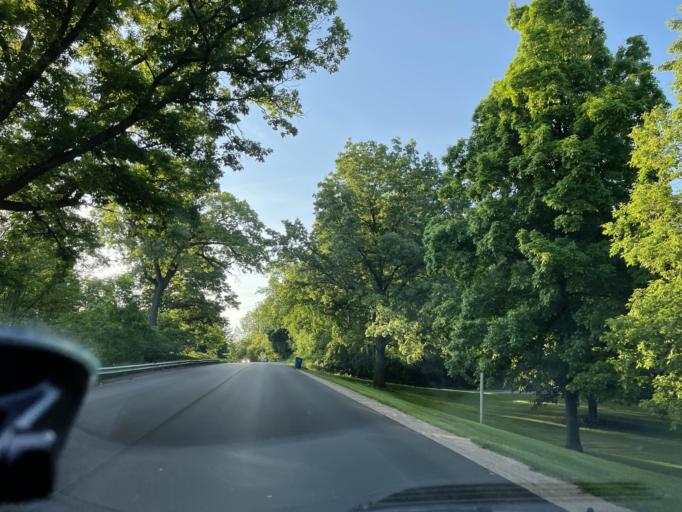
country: US
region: Michigan
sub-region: Barry County
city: Middleville
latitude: 42.7117
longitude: -85.4442
